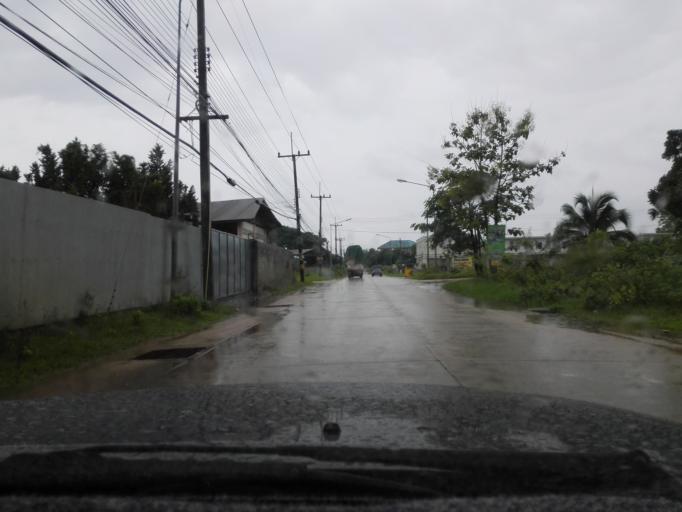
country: TH
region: Tak
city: Mae Sot
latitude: 16.7007
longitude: 98.5730
